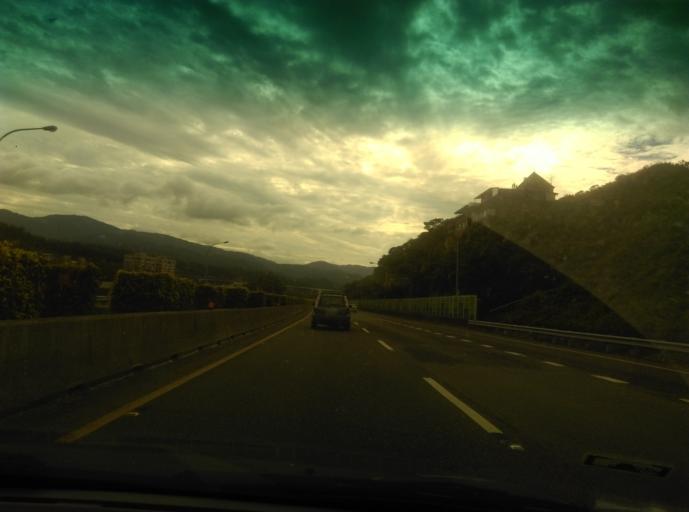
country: TW
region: Taiwan
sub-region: Keelung
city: Keelung
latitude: 25.1139
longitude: 121.7277
